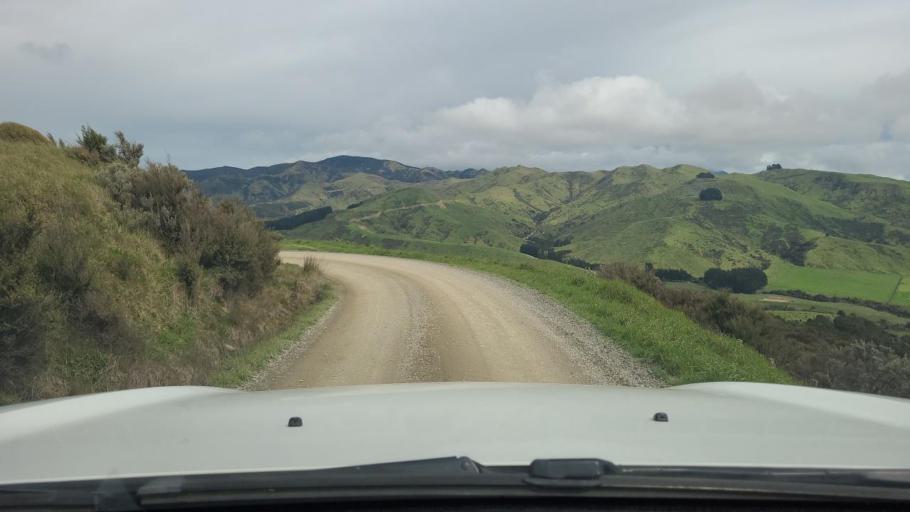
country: NZ
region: Wellington
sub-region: South Wairarapa District
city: Waipawa
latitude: -41.3842
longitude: 175.4670
